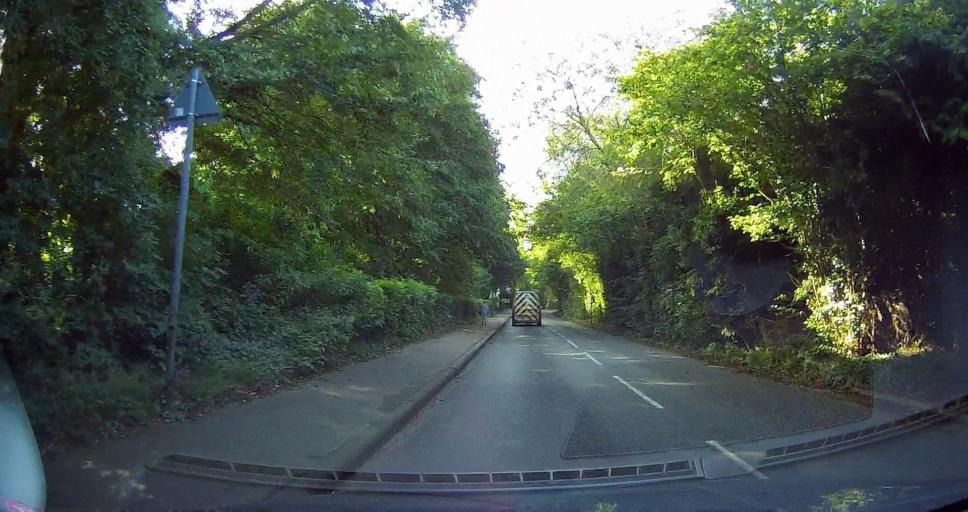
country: GB
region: England
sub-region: Kent
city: Longfield
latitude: 51.3646
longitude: 0.3014
